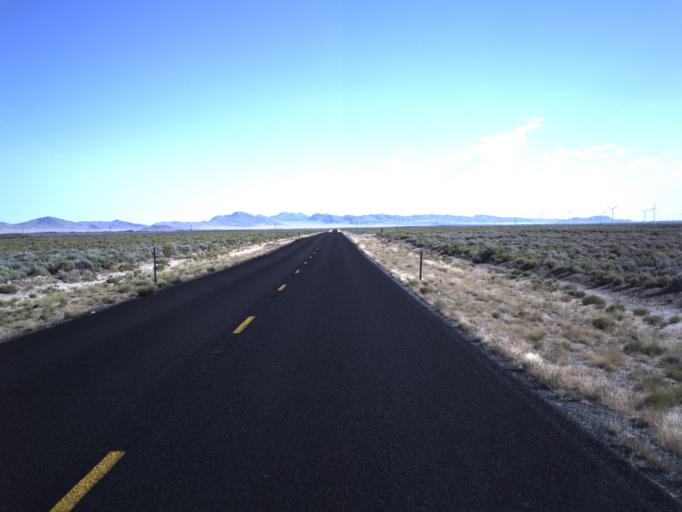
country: US
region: Utah
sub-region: Beaver County
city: Milford
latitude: 38.5376
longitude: -112.9912
